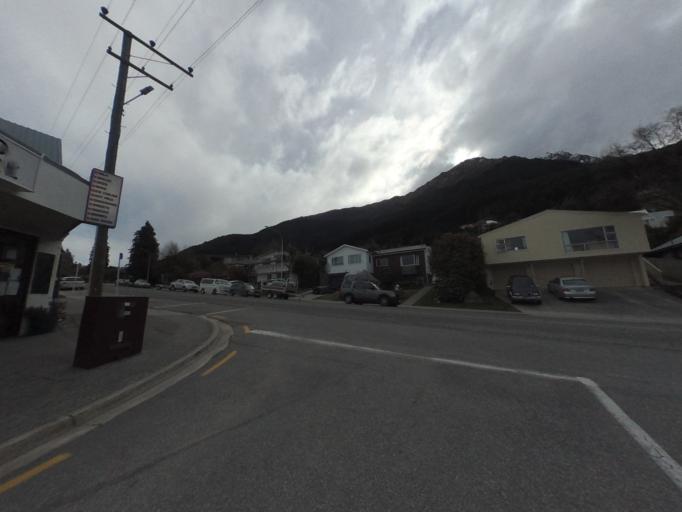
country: NZ
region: Otago
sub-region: Queenstown-Lakes District
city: Queenstown
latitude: -45.0392
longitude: 168.6331
